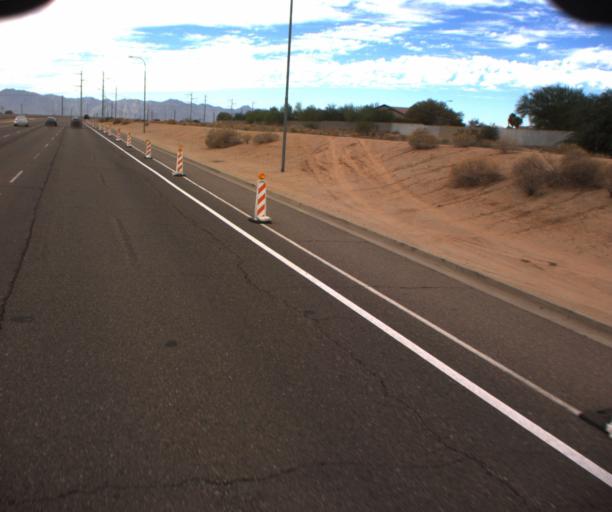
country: US
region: Arizona
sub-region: Maricopa County
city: Guadalupe
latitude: 33.2929
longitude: -111.9850
